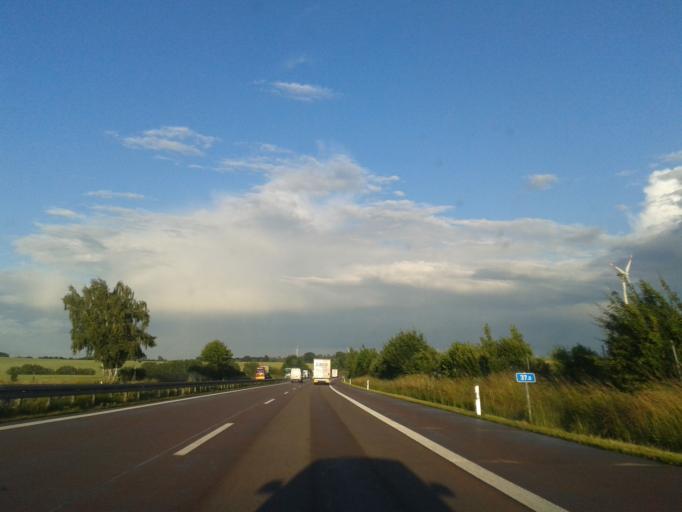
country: DE
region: Saxony
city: Bockelwitz
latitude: 51.2181
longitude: 12.9334
